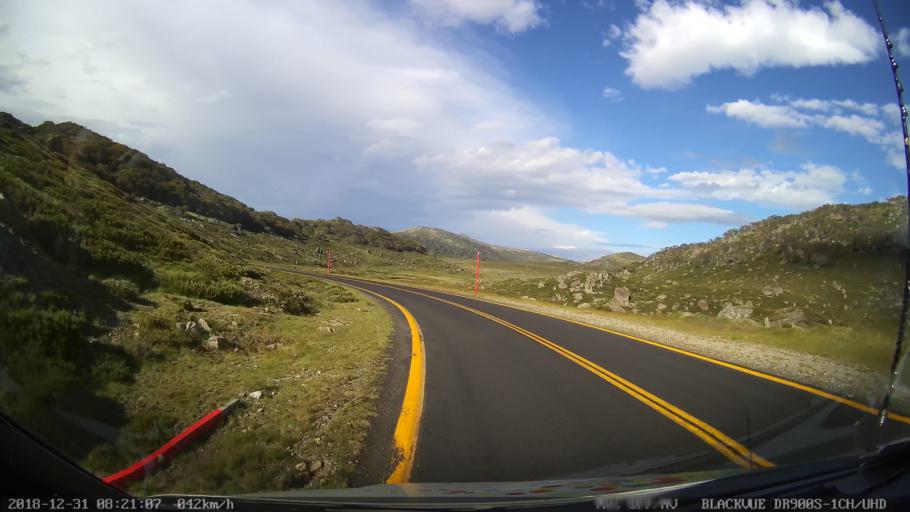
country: AU
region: New South Wales
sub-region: Snowy River
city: Jindabyne
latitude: -36.4263
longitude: 148.3702
